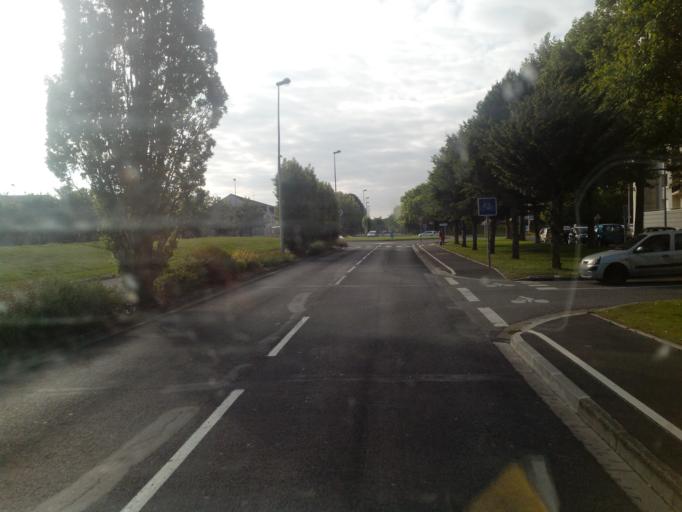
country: FR
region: Lower Normandy
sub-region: Departement du Calvados
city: Saint-Contest
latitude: 49.2003
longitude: -0.3872
